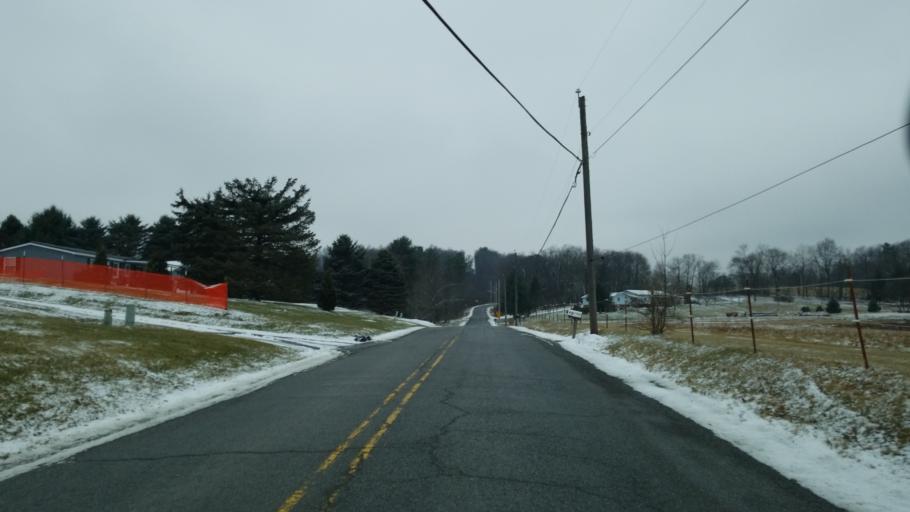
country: US
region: Pennsylvania
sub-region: Clearfield County
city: Sandy
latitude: 41.0784
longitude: -78.7923
